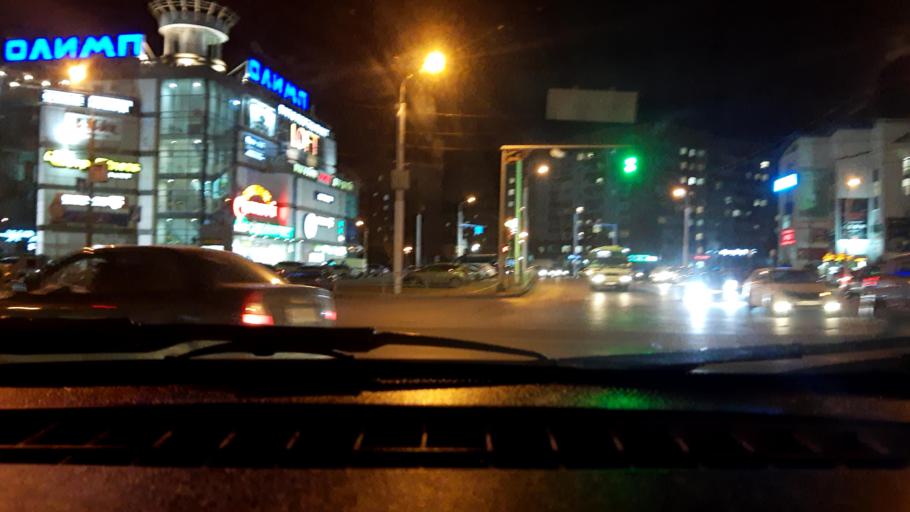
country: RU
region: Bashkortostan
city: Ufa
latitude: 54.7656
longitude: 56.0490
